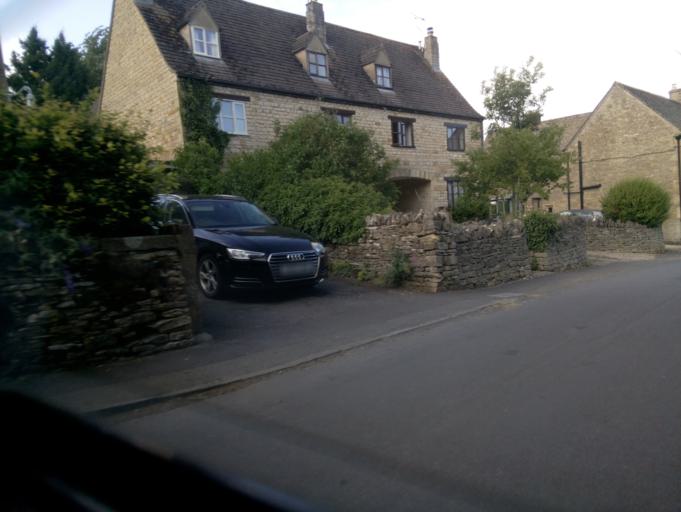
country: GB
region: England
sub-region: Gloucestershire
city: Westfield
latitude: 51.9096
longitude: -1.8320
